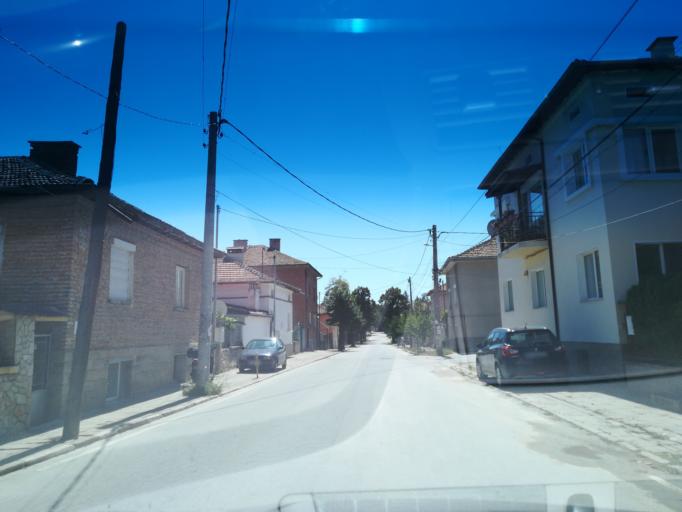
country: BG
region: Pazardzhik
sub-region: Obshtina Strelcha
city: Strelcha
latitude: 42.5106
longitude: 24.3201
